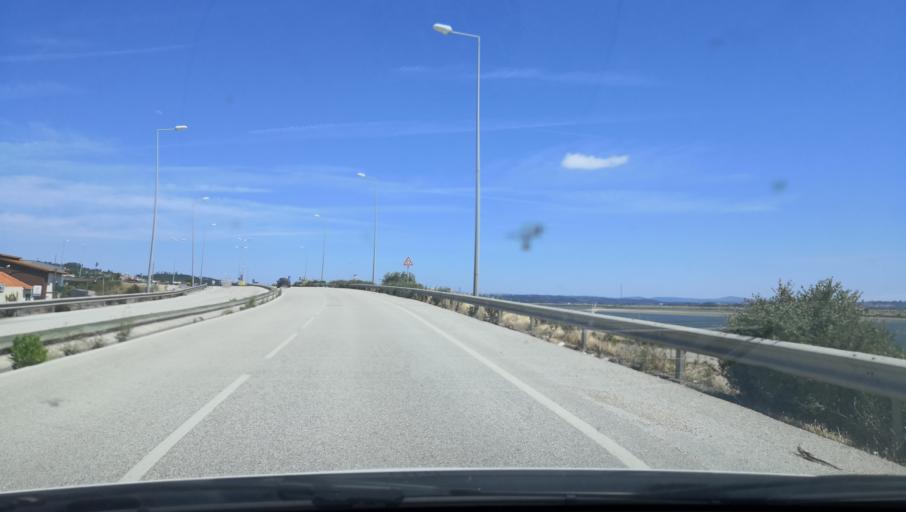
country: PT
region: Coimbra
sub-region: Figueira da Foz
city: Tavarede
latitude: 40.1474
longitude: -8.8353
